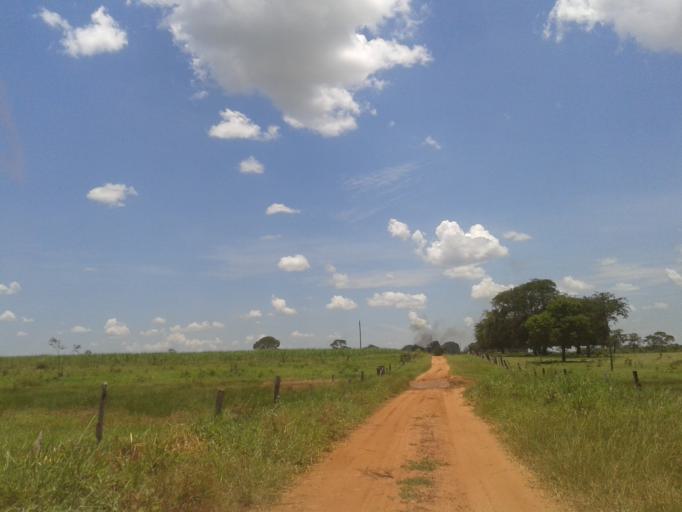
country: BR
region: Minas Gerais
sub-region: Santa Vitoria
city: Santa Vitoria
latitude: -19.2260
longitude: -50.4617
